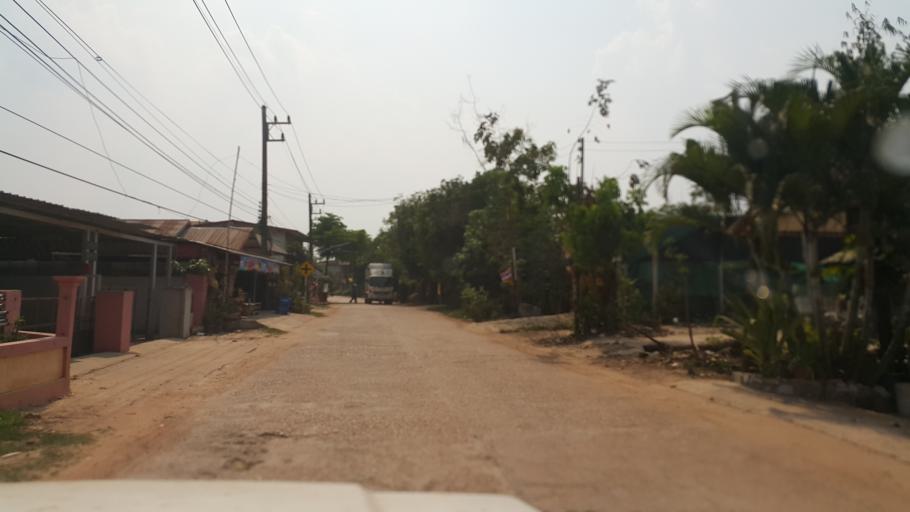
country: TH
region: Nakhon Phanom
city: Ban Phaeng
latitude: 17.9626
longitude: 104.1934
